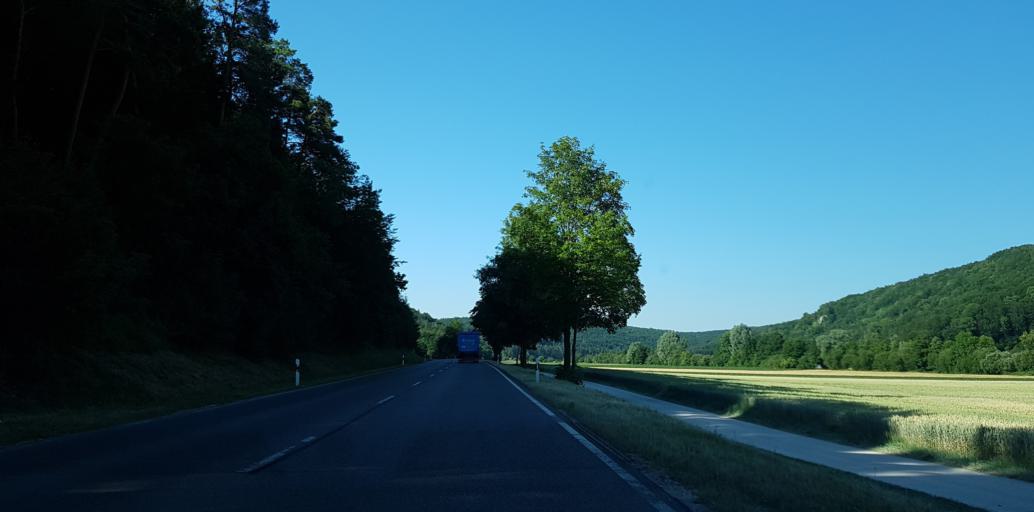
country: DE
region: Baden-Wuerttemberg
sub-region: Tuebingen Region
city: Schelklingen
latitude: 48.3593
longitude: 9.7196
